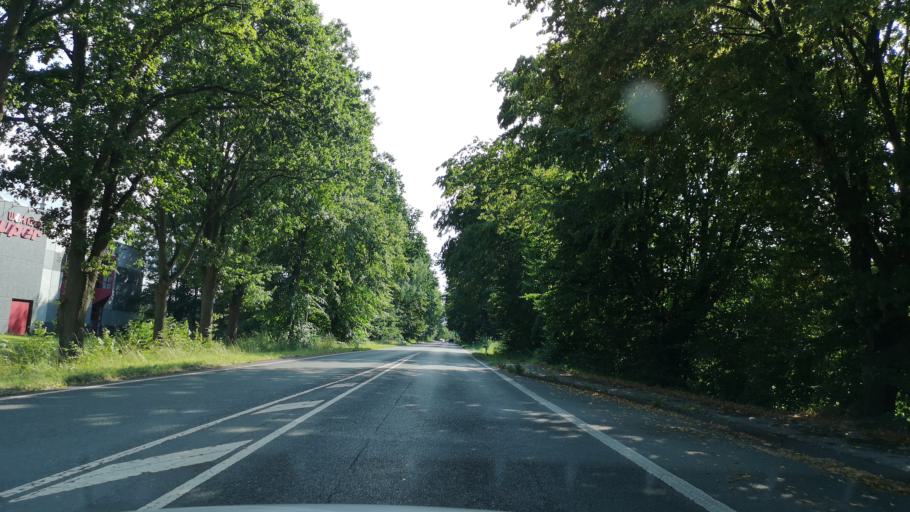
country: DE
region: North Rhine-Westphalia
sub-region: Regierungsbezirk Arnsberg
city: Holzwickede
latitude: 51.4604
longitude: 7.6171
